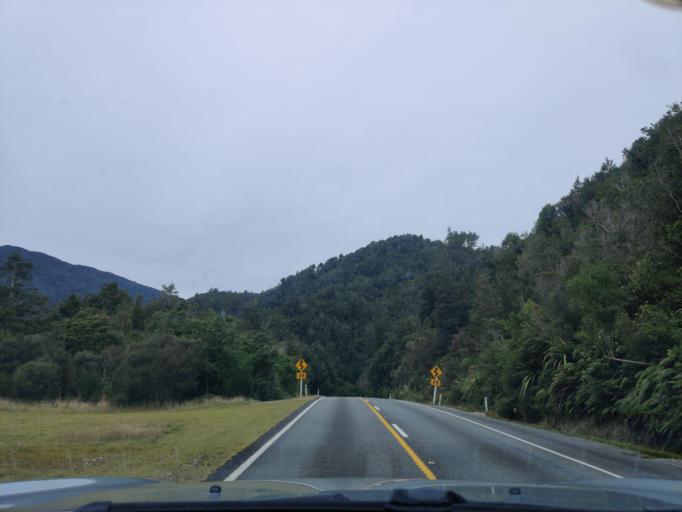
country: NZ
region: West Coast
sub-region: Buller District
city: Westport
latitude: -41.8486
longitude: 171.7275
